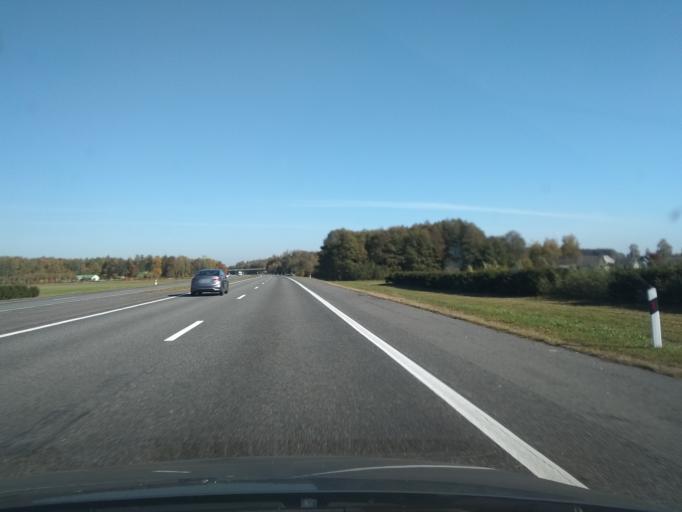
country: BY
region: Brest
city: Ivatsevichy
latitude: 52.6738
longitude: 25.3142
